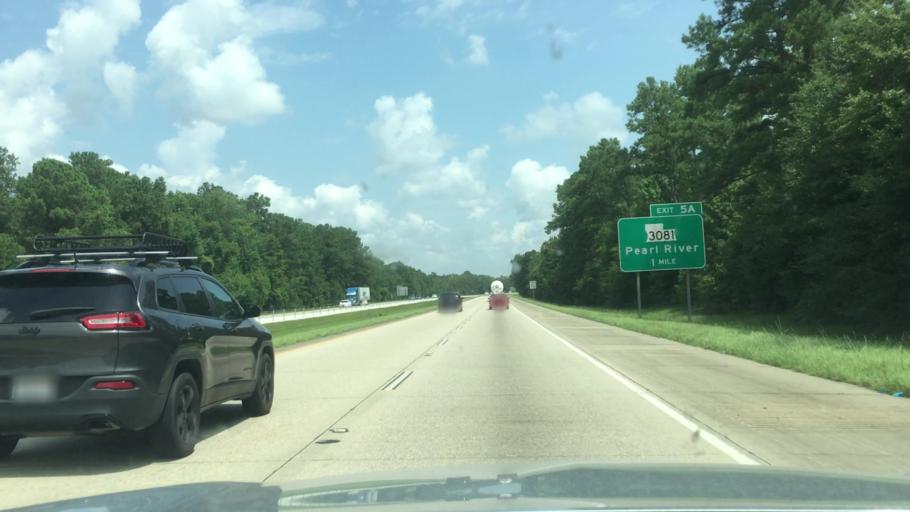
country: US
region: Louisiana
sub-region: Saint Tammany Parish
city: Pearl River
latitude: 30.3607
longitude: -89.7419
